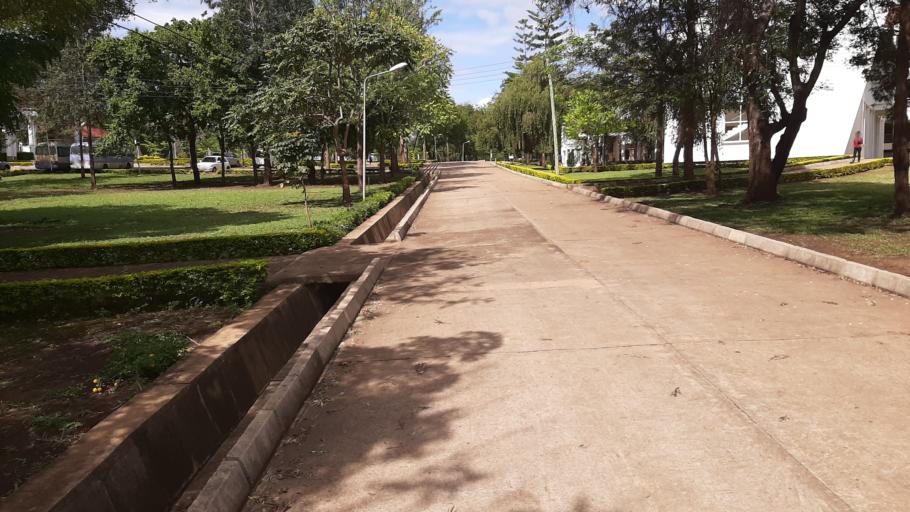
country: TZ
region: Arusha
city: Usa River
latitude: -3.4001
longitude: 36.7959
